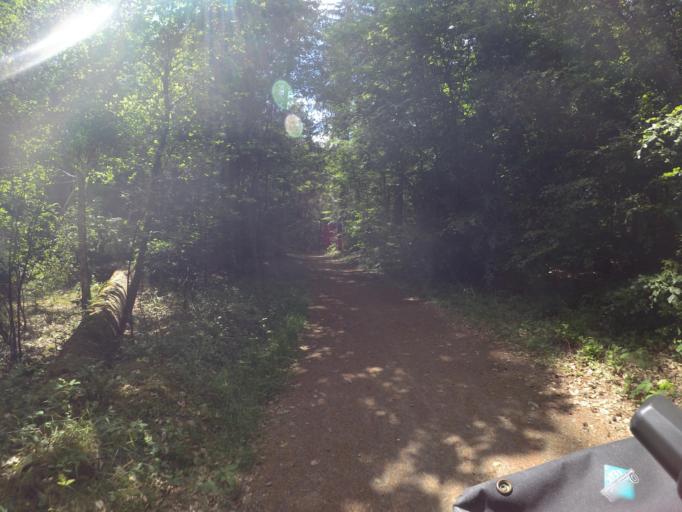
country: DE
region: Rheinland-Pfalz
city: Rodenbach
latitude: 49.4649
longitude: 7.6777
